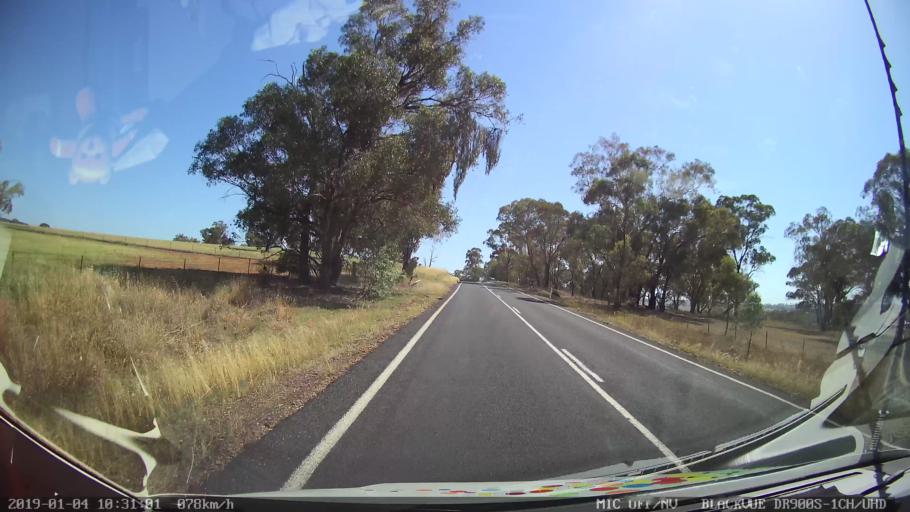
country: AU
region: New South Wales
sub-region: Cabonne
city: Canowindra
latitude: -33.3395
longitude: 148.6308
